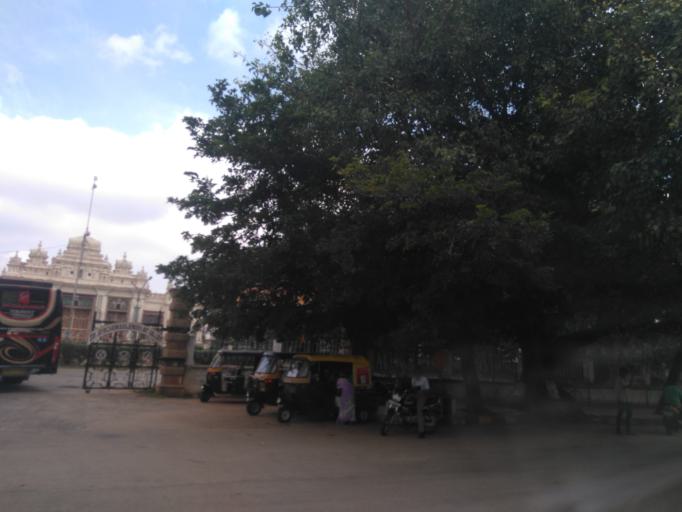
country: IN
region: Karnataka
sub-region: Mysore
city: Mysore
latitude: 12.3066
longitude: 76.6510
